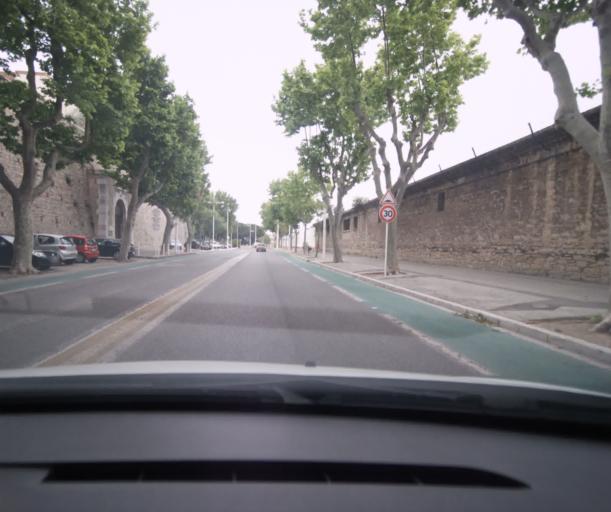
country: FR
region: Provence-Alpes-Cote d'Azur
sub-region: Departement du Var
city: Toulon
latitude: 43.1096
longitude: 5.9315
